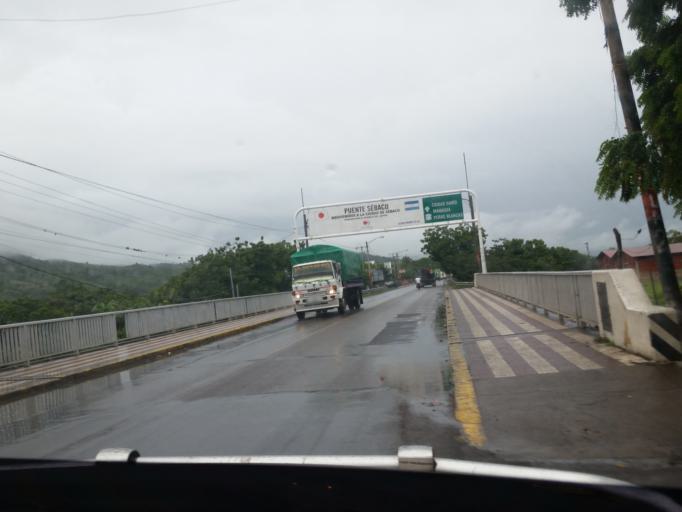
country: NI
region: Matagalpa
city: Ciudad Dario
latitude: 12.8496
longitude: -86.0997
